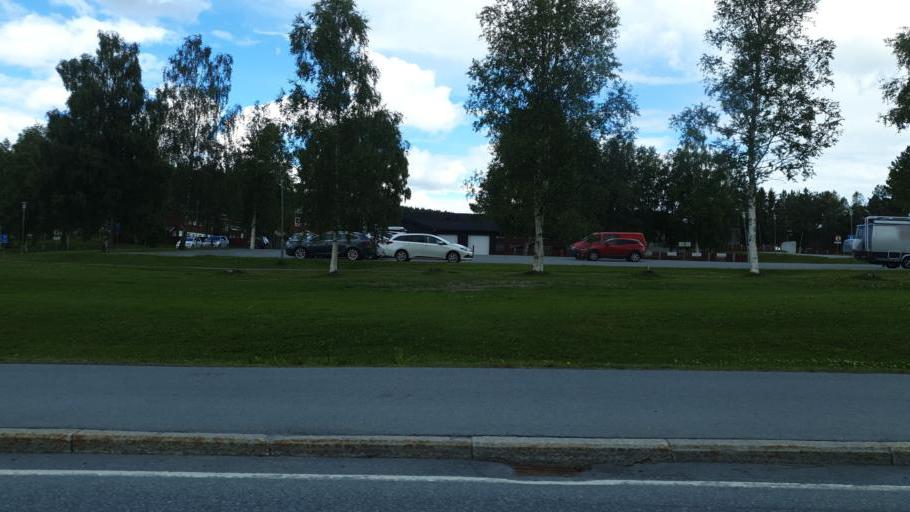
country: NO
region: Sor-Trondelag
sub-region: Rennebu
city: Berkak
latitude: 62.8282
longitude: 10.0062
